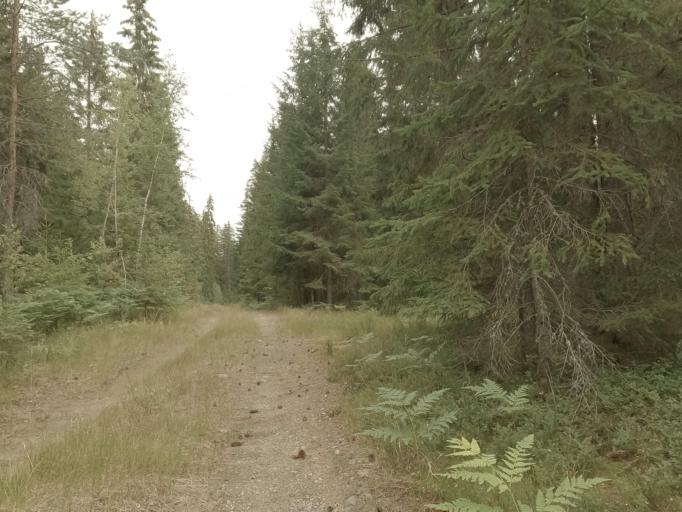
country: RU
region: Leningrad
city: Kamennogorsk
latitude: 61.0209
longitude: 29.1701
